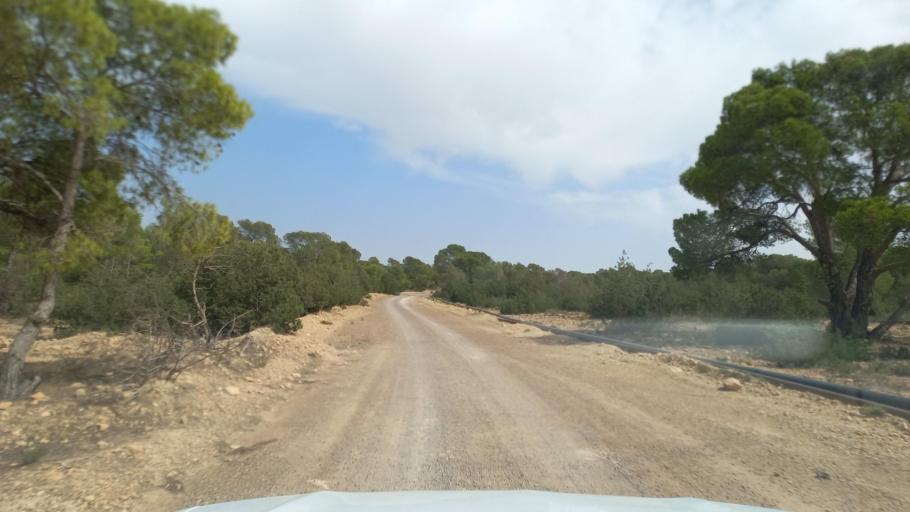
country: TN
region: Al Qasrayn
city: Kasserine
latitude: 35.3821
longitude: 8.8885
